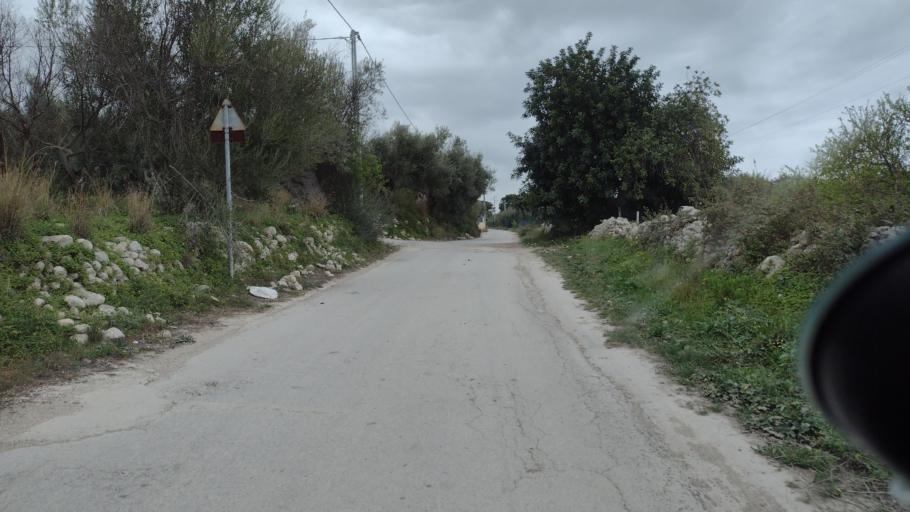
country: IT
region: Sicily
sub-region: Provincia di Siracusa
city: Avola
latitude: 36.9044
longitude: 15.1120
